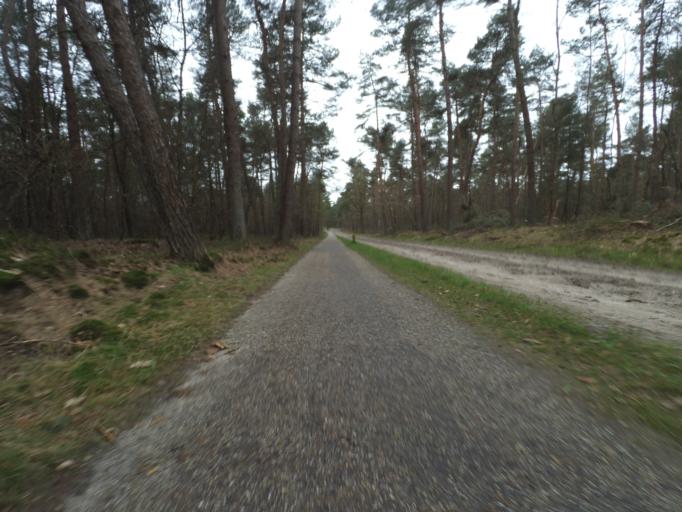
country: NL
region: Gelderland
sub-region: Gemeente Apeldoorn
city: Loenen
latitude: 52.0954
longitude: 6.0214
